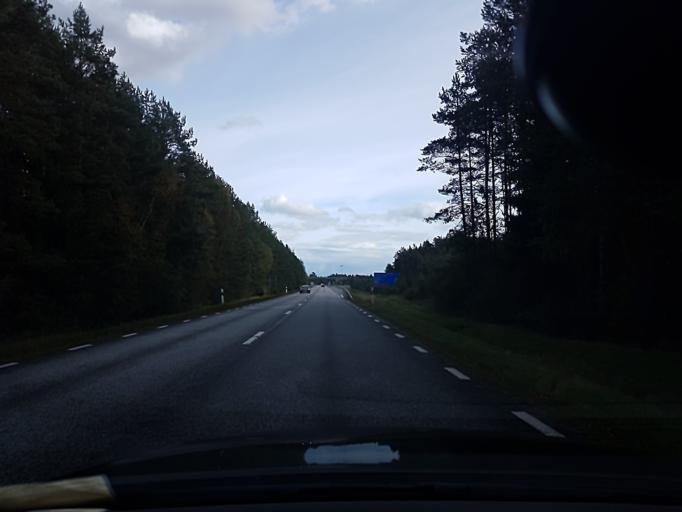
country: SE
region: Joenkoeping
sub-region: Varnamo Kommun
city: Bredaryd
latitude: 57.1830
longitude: 13.7415
